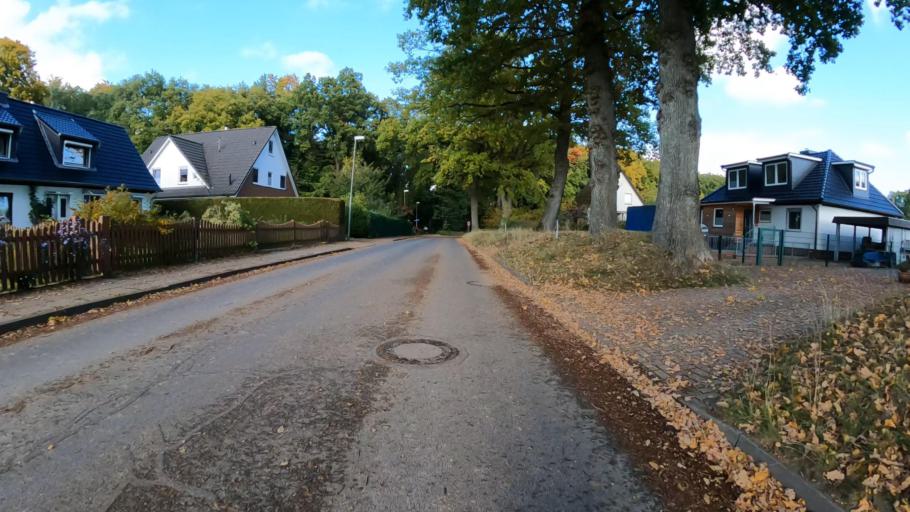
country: DE
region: Schleswig-Holstein
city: Ahrensburg
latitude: 53.6445
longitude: 10.2188
